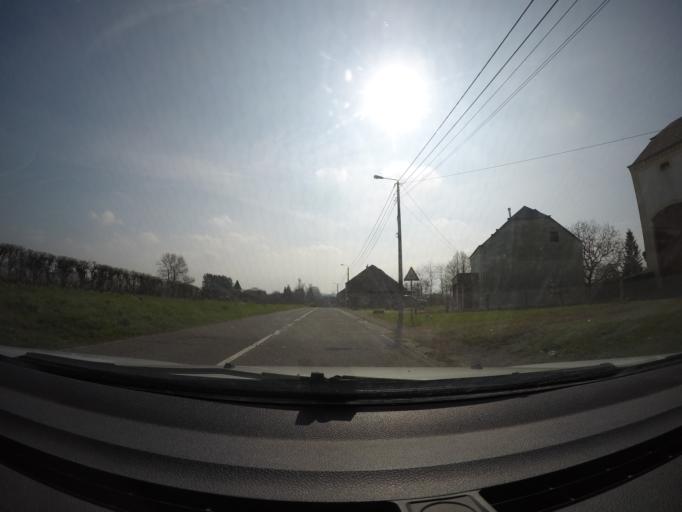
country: BE
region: Wallonia
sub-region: Province du Luxembourg
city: Tintigny
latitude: 49.7165
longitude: 5.5164
